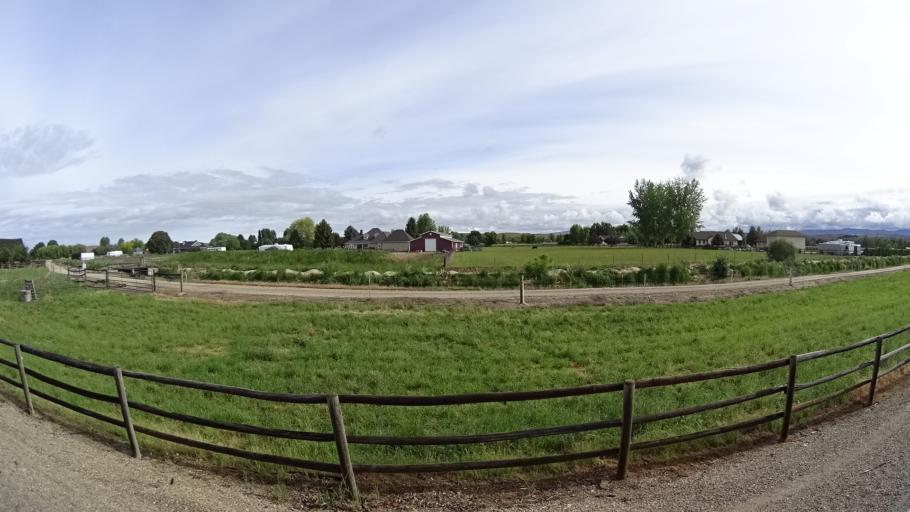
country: US
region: Idaho
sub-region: Ada County
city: Eagle
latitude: 43.7208
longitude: -116.3819
